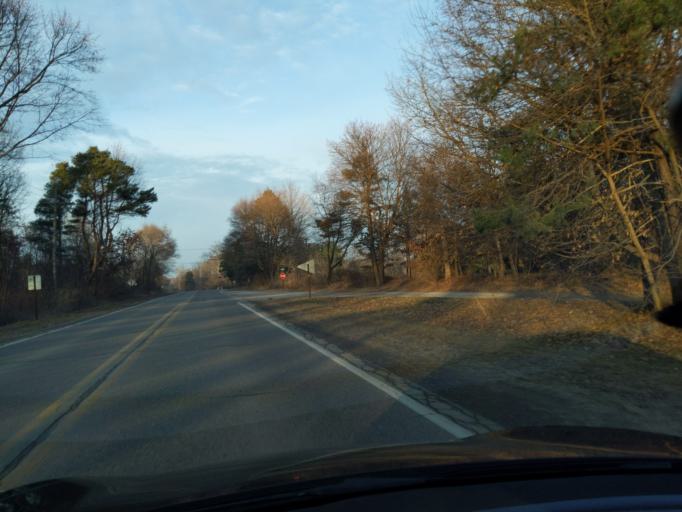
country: US
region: Michigan
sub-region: Livingston County
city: Brighton
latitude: 42.5637
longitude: -83.7544
